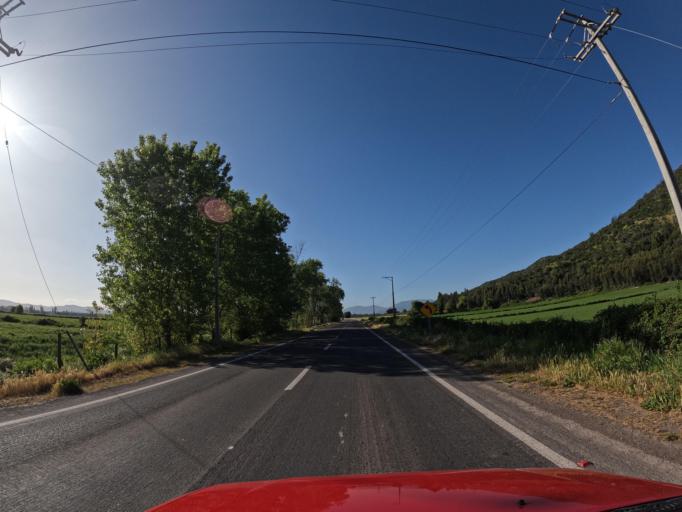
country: CL
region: Maule
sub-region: Provincia de Curico
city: Teno
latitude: -34.7765
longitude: -71.2310
